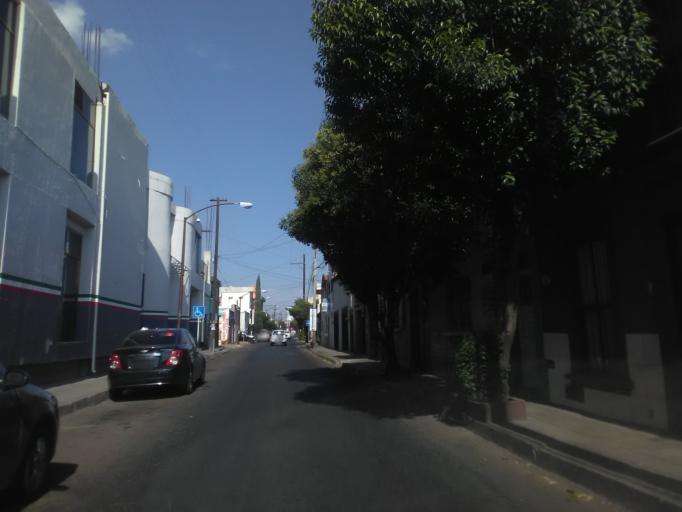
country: MX
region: Durango
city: Victoria de Durango
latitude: 24.0282
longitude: -104.6619
